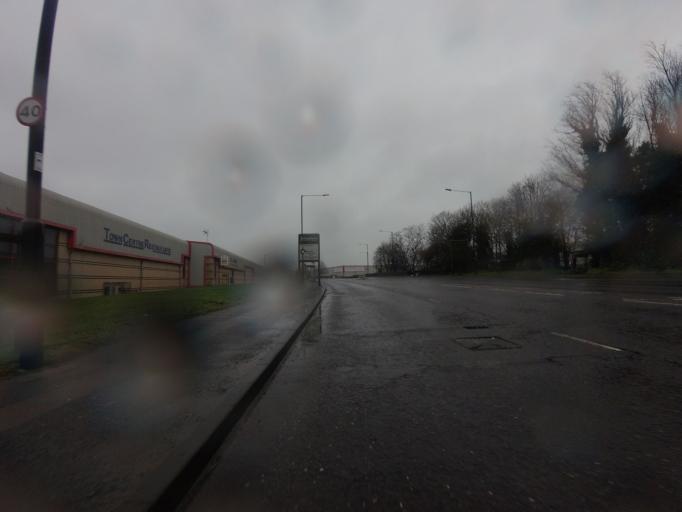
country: GB
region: England
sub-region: Hertfordshire
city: Waltham Cross
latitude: 51.6531
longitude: -0.0288
